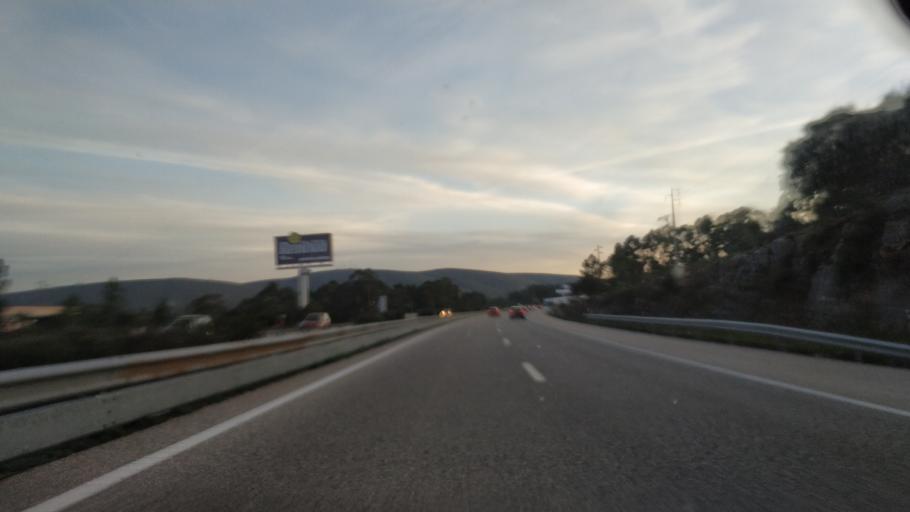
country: PT
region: Santarem
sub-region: Ourem
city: Fatima
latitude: 39.5730
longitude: -8.6528
